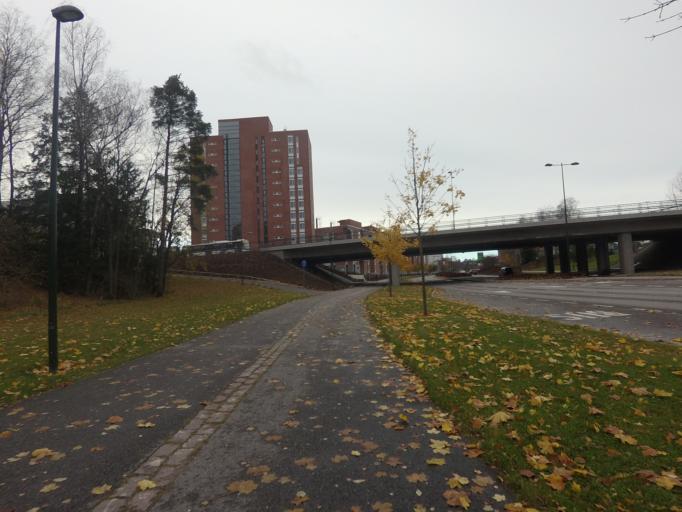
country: FI
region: Uusimaa
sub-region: Helsinki
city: Koukkuniemi
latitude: 60.1659
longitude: 24.7376
